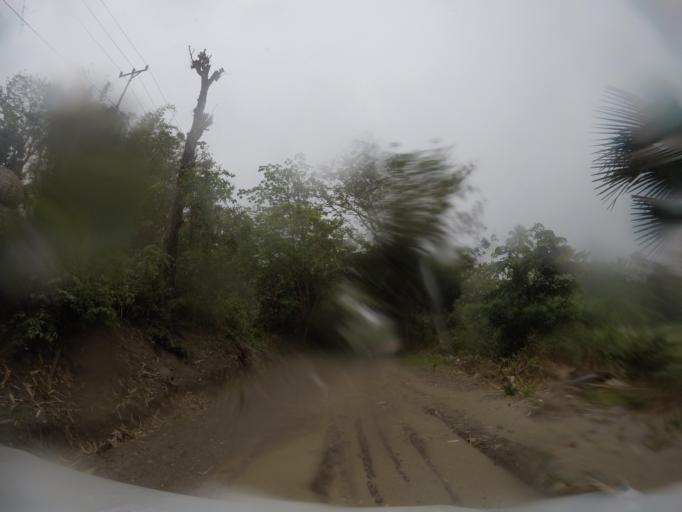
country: TL
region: Baucau
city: Venilale
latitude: -8.6322
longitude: 126.4428
